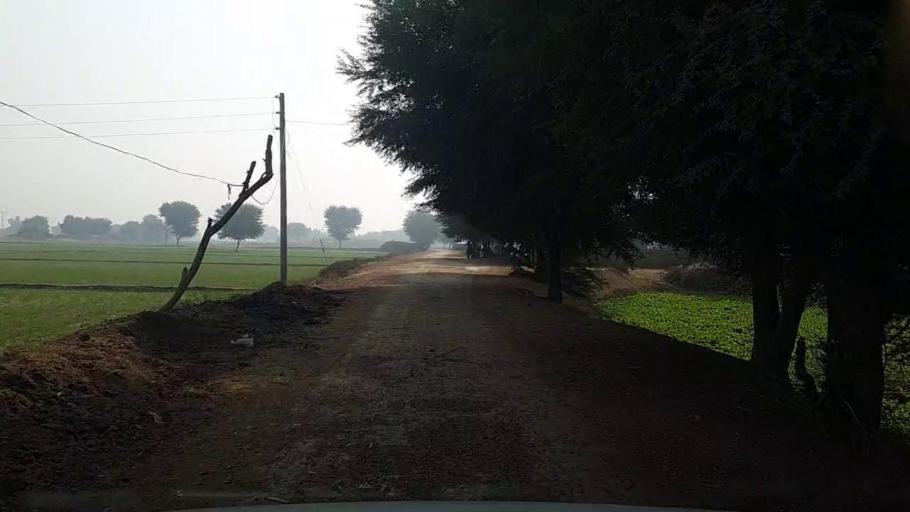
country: PK
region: Sindh
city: Setharja Old
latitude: 27.1512
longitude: 68.4659
